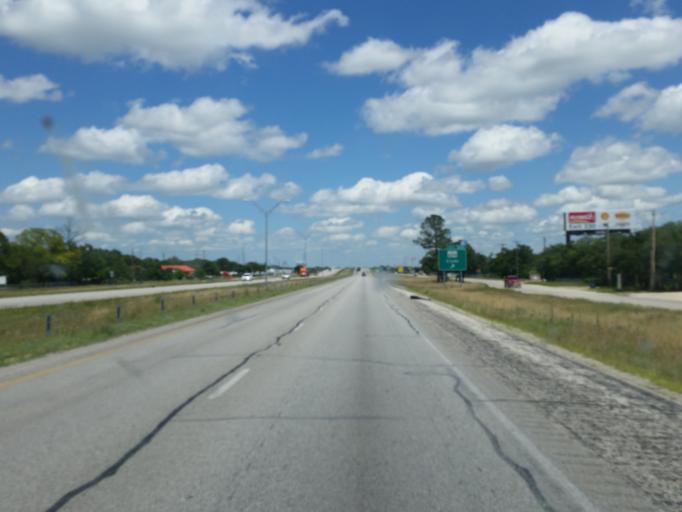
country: US
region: Texas
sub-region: Callahan County
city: Clyde
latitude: 32.4164
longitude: -99.5158
